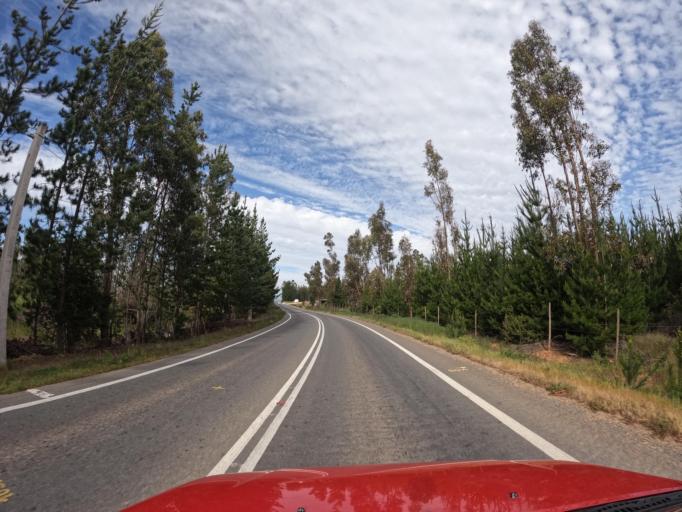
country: CL
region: O'Higgins
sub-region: Provincia de Colchagua
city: Santa Cruz
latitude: -34.3105
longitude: -71.8451
